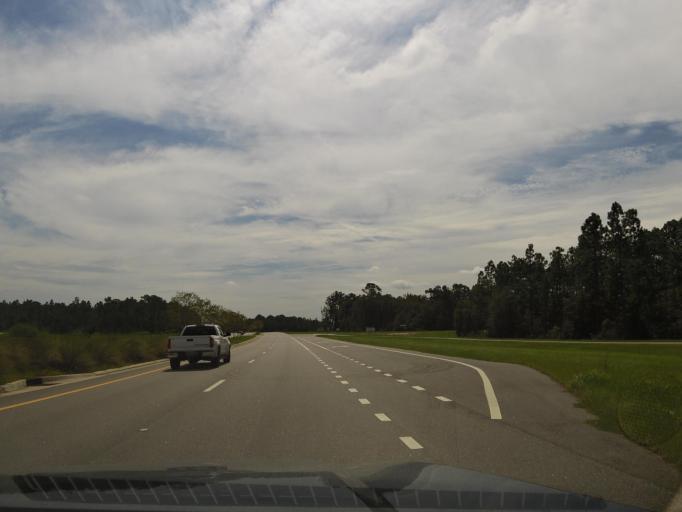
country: US
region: Florida
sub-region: Saint Johns County
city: Fruit Cove
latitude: 30.0288
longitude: -81.5250
